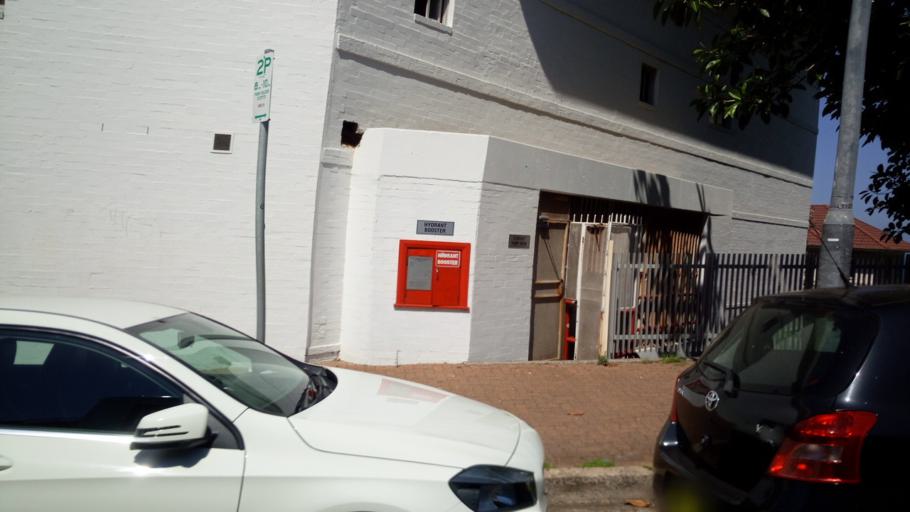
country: AU
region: New South Wales
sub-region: Waverley
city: Bondi Beach
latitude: -33.8947
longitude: 151.2733
